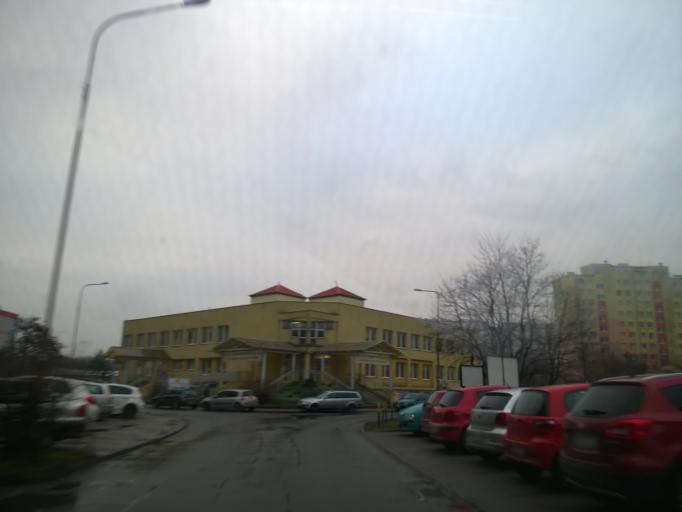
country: PL
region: Lower Silesian Voivodeship
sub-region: Powiat wroclawski
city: Wroclaw
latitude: 51.0792
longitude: 17.0473
